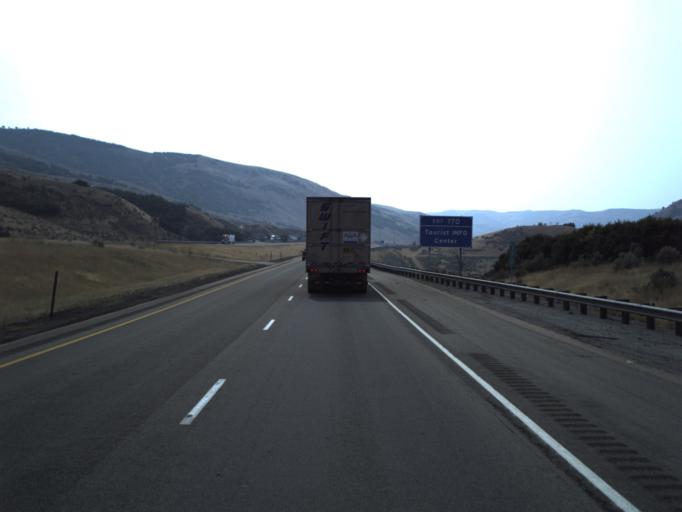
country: US
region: Utah
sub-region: Summit County
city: Coalville
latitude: 40.9948
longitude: -111.3983
